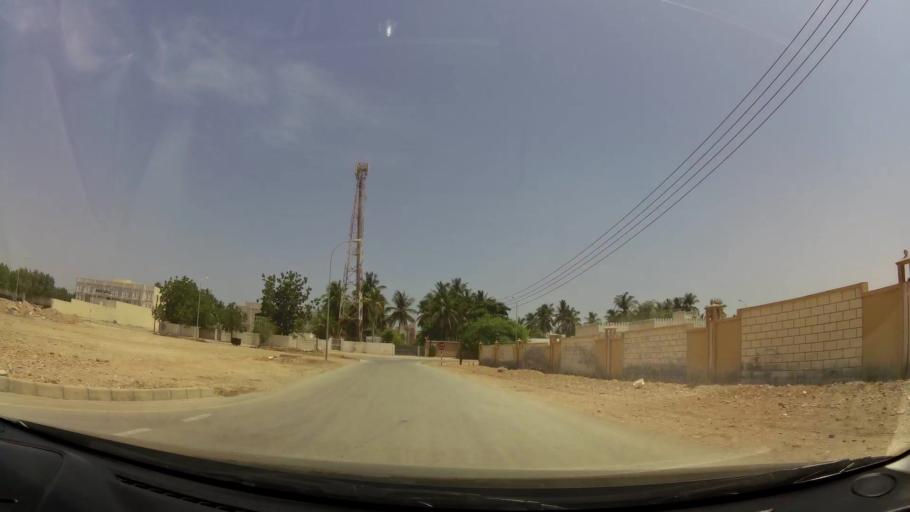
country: OM
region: Zufar
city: Salalah
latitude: 17.0633
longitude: 54.1537
